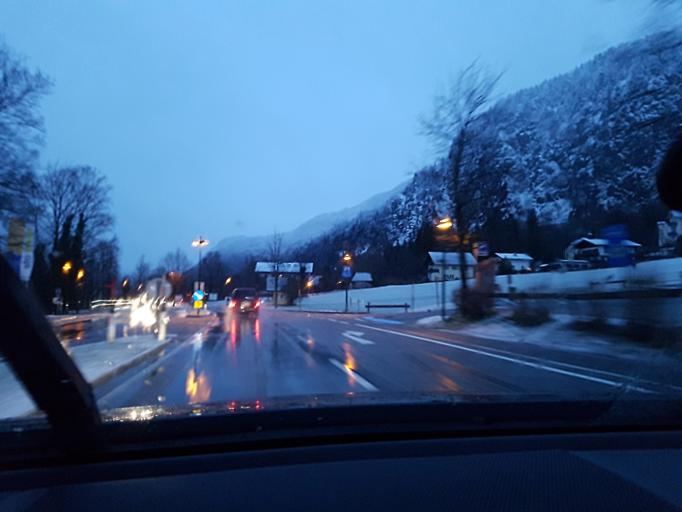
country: AT
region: Salzburg
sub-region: Politischer Bezirk Salzburg-Umgebung
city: Sankt Gilgen
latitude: 47.7637
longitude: 13.3651
